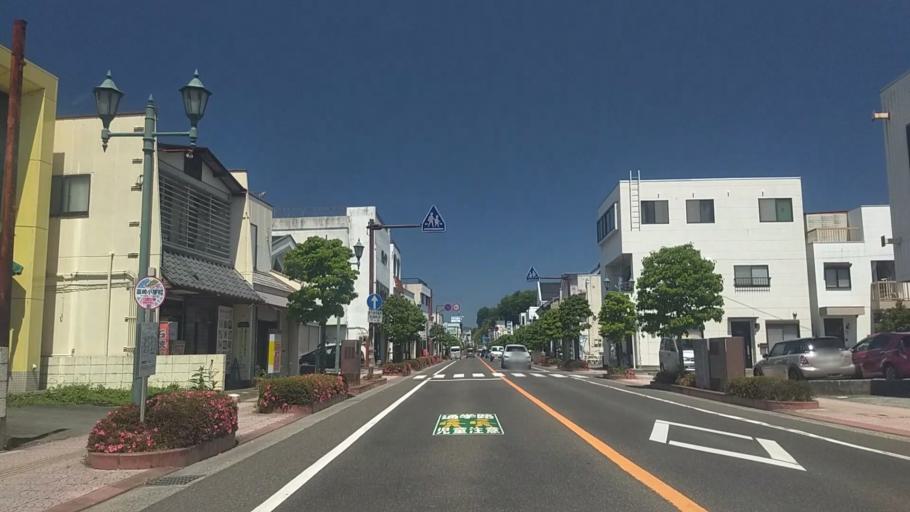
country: JP
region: Yamanashi
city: Nirasaki
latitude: 35.7053
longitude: 138.4526
